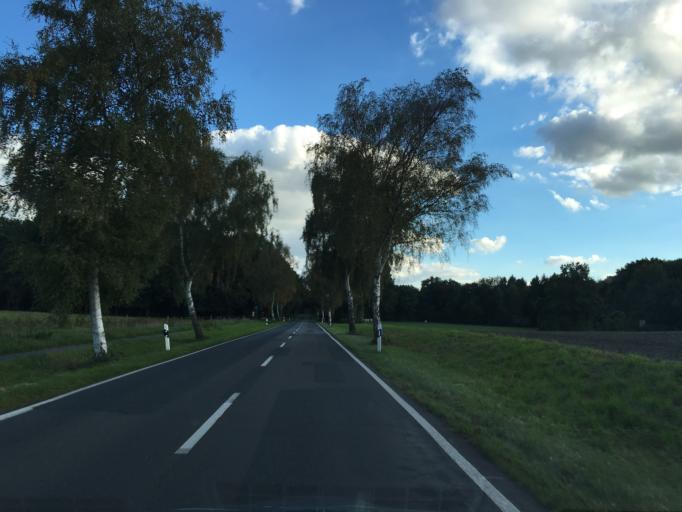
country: DE
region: Lower Saxony
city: Vierhofen
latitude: 53.2559
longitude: 10.2236
